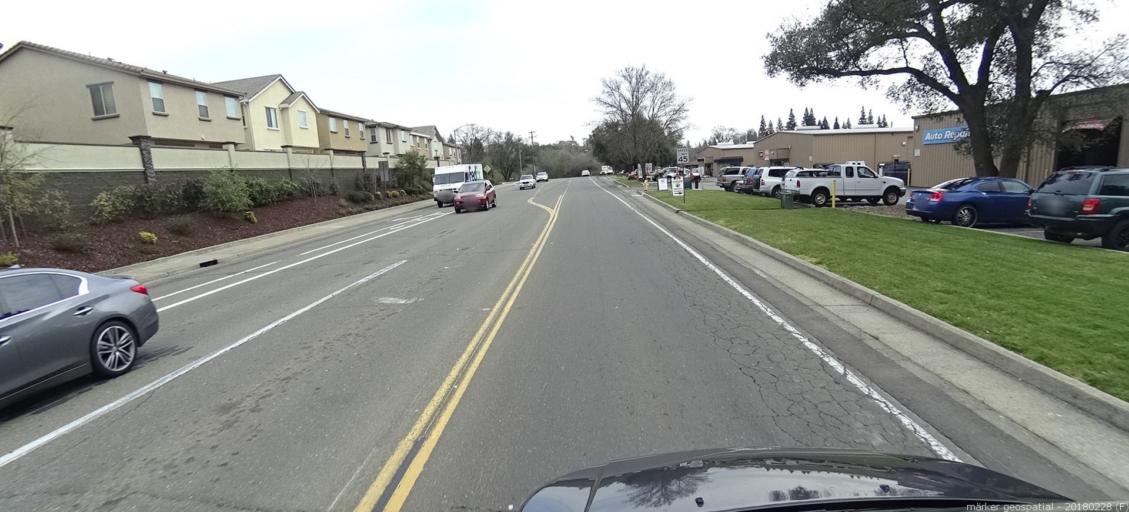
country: US
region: California
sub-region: Sacramento County
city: Folsom
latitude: 38.6633
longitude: -121.1717
